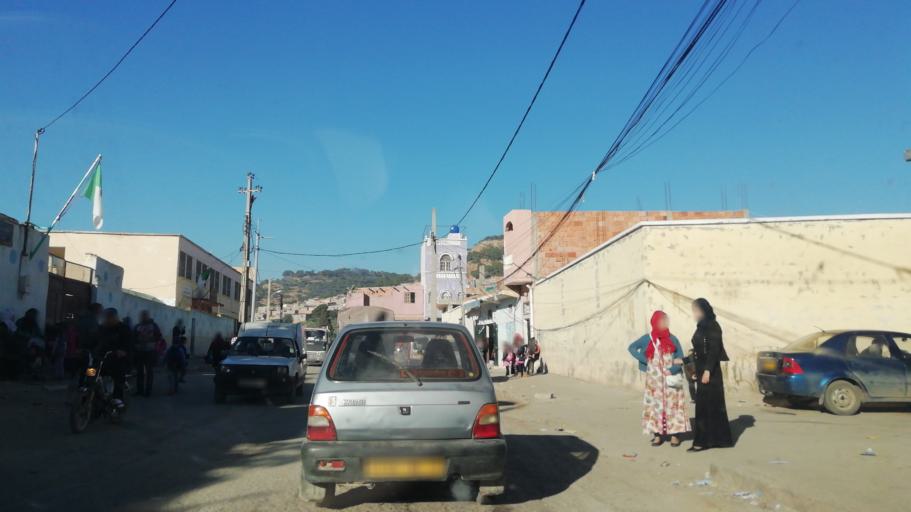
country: DZ
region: Oran
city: Oran
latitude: 35.6861
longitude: -0.6717
